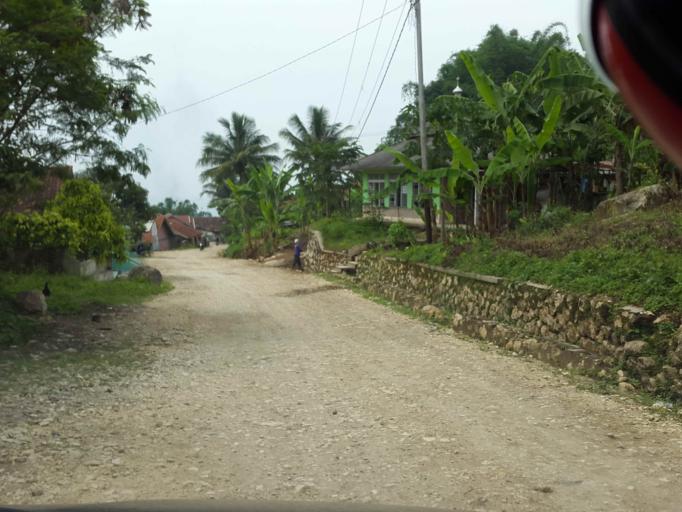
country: ID
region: West Java
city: Padalarang
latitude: -6.8418
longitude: 107.4209
